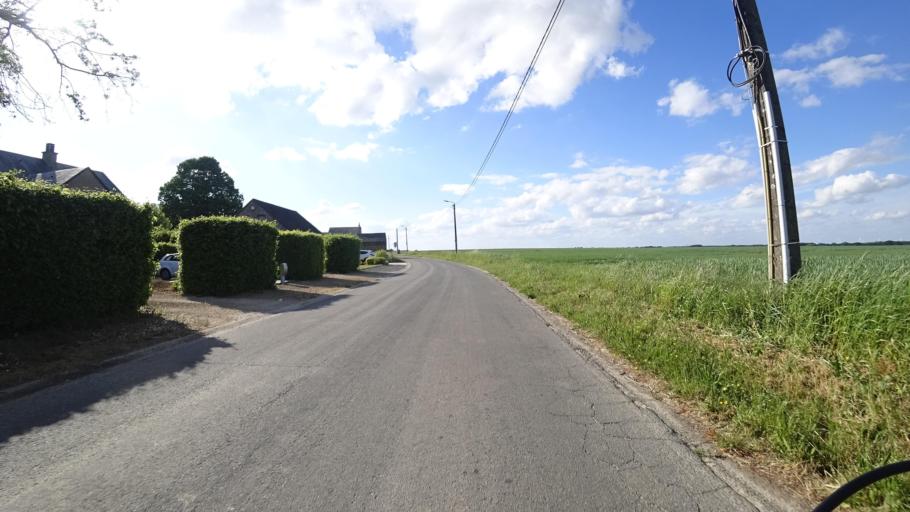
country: BE
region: Wallonia
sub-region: Province de Namur
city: Gembloux
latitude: 50.5356
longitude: 4.7498
